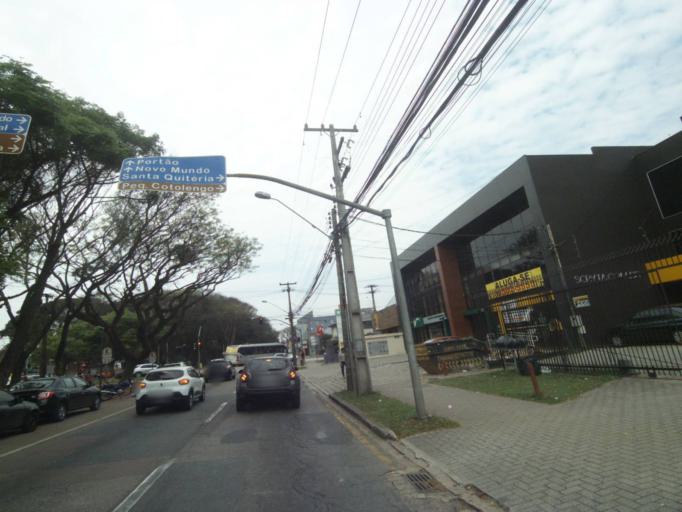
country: BR
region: Parana
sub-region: Curitiba
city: Curitiba
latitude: -25.4546
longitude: -49.3041
